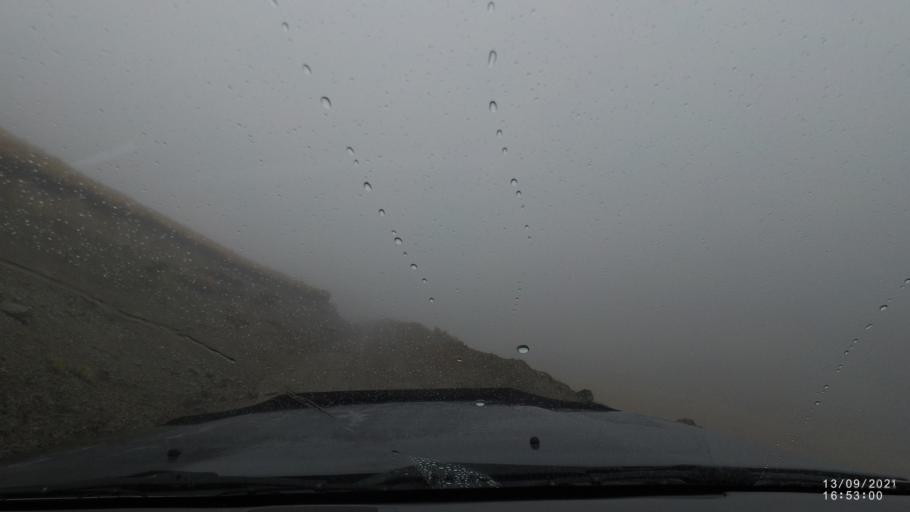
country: BO
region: Cochabamba
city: Colomi
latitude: -17.3053
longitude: -65.7096
